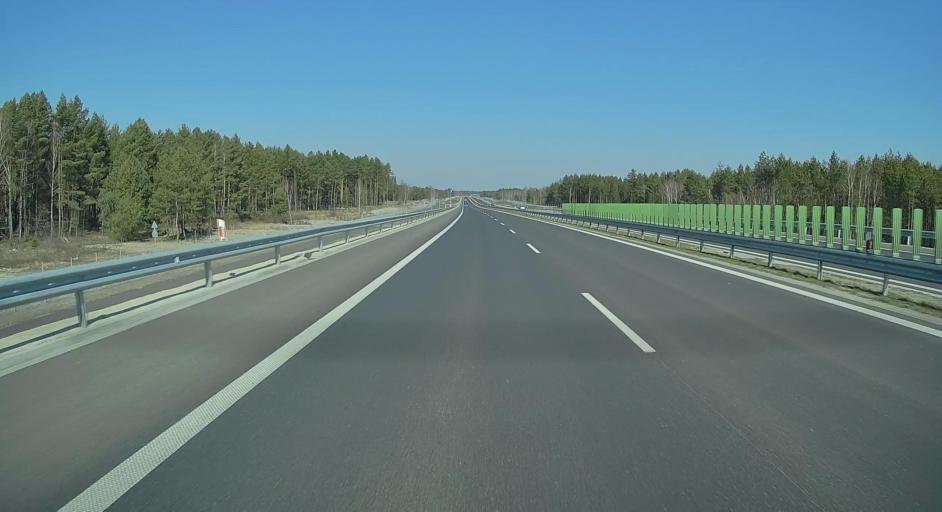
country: PL
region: Subcarpathian Voivodeship
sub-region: Powiat nizanski
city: Konczyce
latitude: 50.4402
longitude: 22.1402
